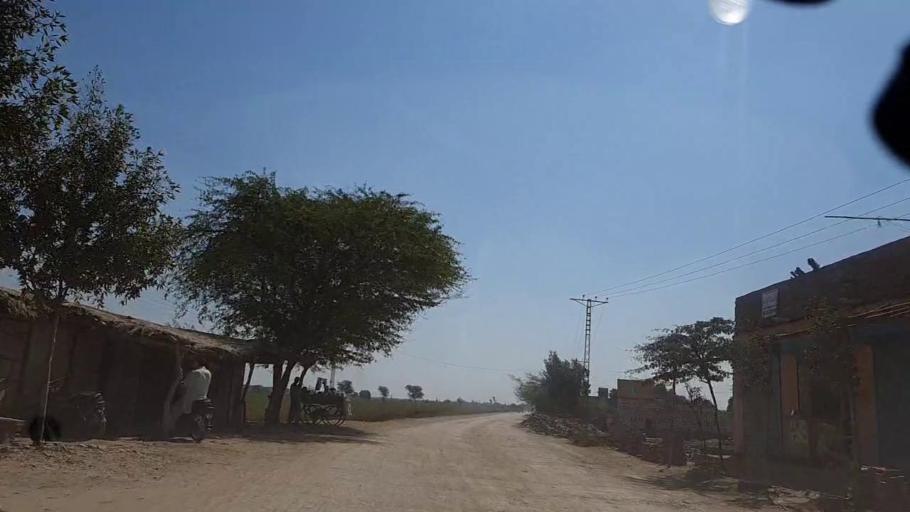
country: PK
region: Sindh
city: Mirpur Khas
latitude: 25.5047
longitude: 69.0321
